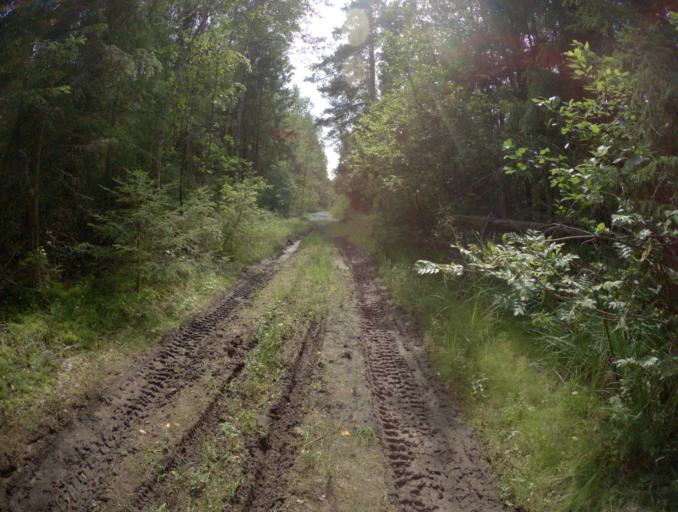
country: RU
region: Vladimir
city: Vorsha
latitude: 55.9551
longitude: 40.1856
